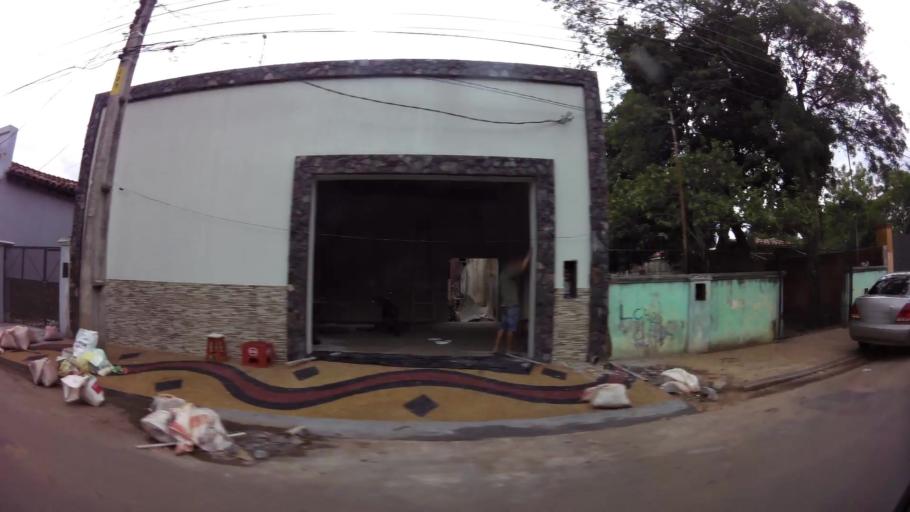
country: PY
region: Central
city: San Lorenzo
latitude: -25.2714
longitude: -57.4954
